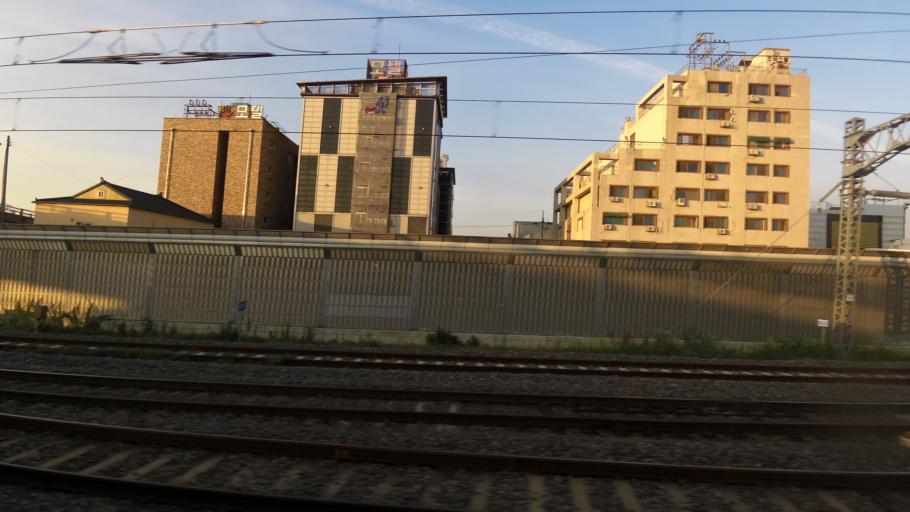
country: KR
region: Chungcheongnam-do
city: Seonghwan
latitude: 36.9948
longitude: 127.0817
